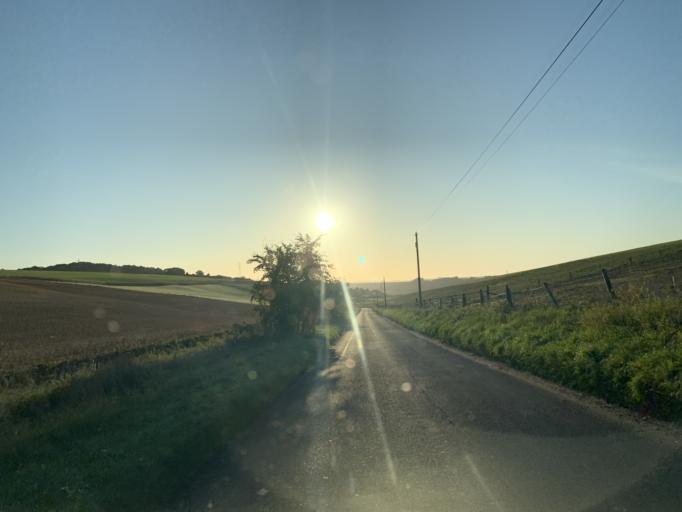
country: GB
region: England
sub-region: Wiltshire
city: Woodford
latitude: 51.1278
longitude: -1.8503
